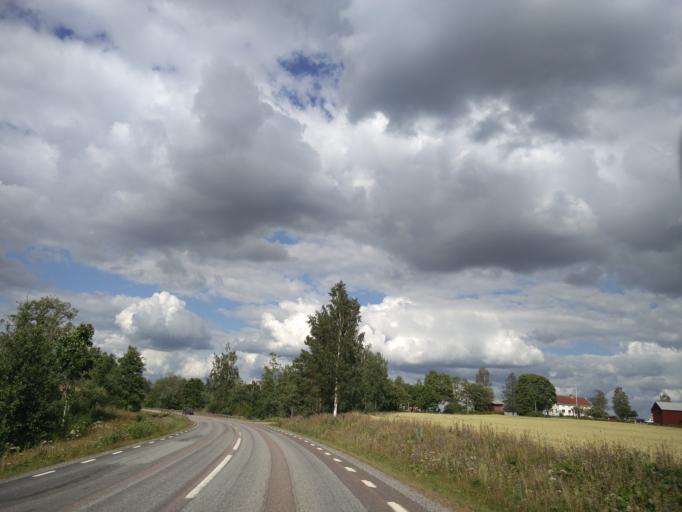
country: SE
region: Vaermland
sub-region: Sunne Kommun
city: Sunne
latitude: 59.7224
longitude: 13.1168
